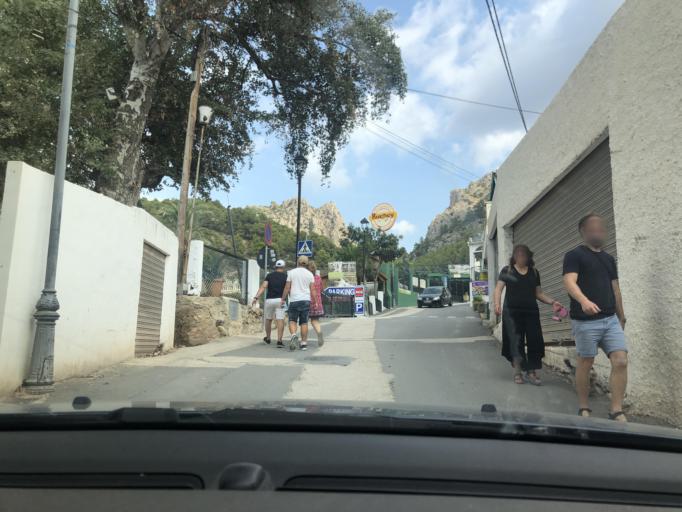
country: ES
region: Valencia
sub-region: Provincia de Alicante
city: Callosa d'En Sarria
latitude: 38.6590
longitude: -0.0968
